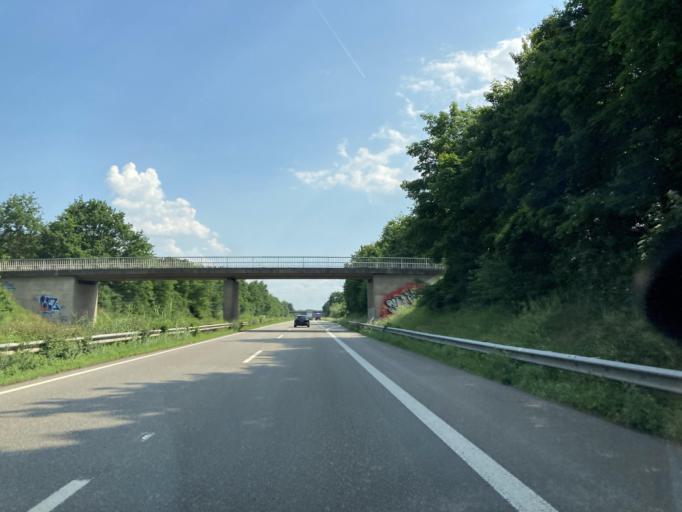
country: DE
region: Rheinland-Pfalz
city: Neupotz
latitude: 49.1285
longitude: 8.3064
